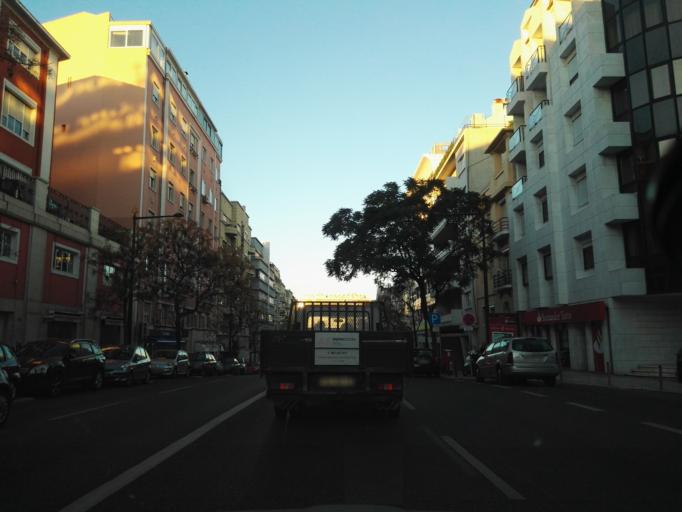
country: PT
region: Lisbon
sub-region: Lisbon
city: Lisbon
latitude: 38.7177
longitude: -9.1573
